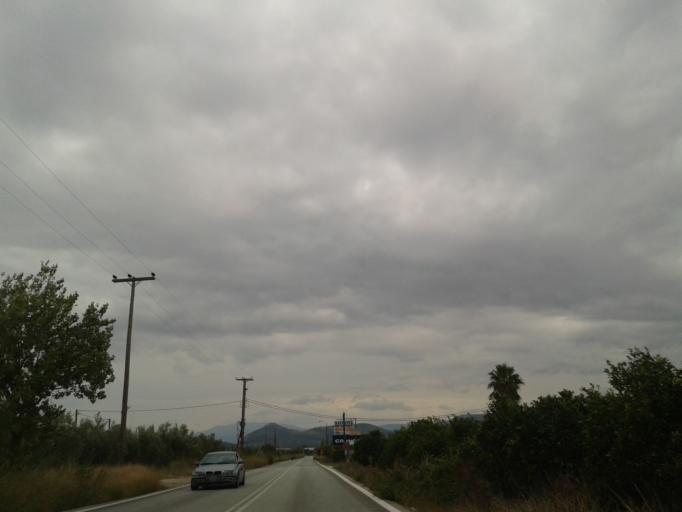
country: GR
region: Peloponnese
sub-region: Nomos Argolidos
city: Koutsopodi
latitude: 37.7050
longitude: 22.7240
